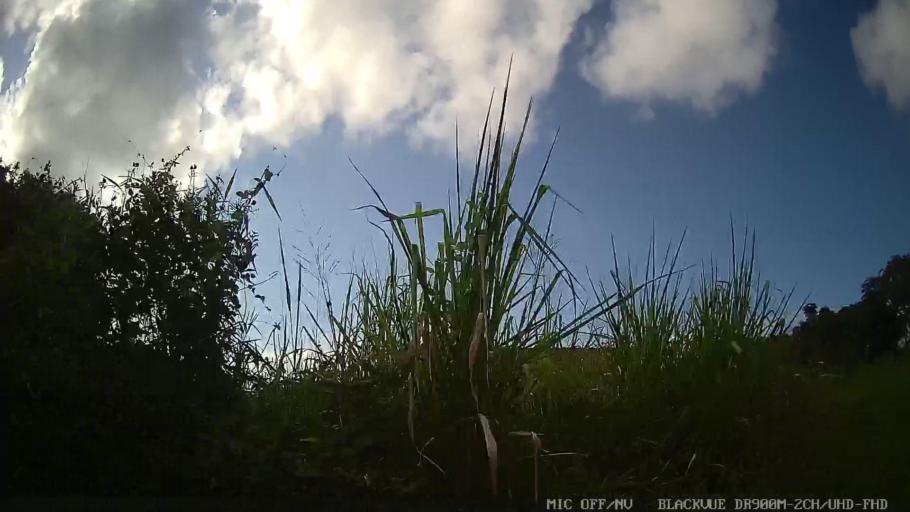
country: BR
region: Sao Paulo
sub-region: Peruibe
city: Peruibe
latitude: -24.2704
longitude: -46.9439
